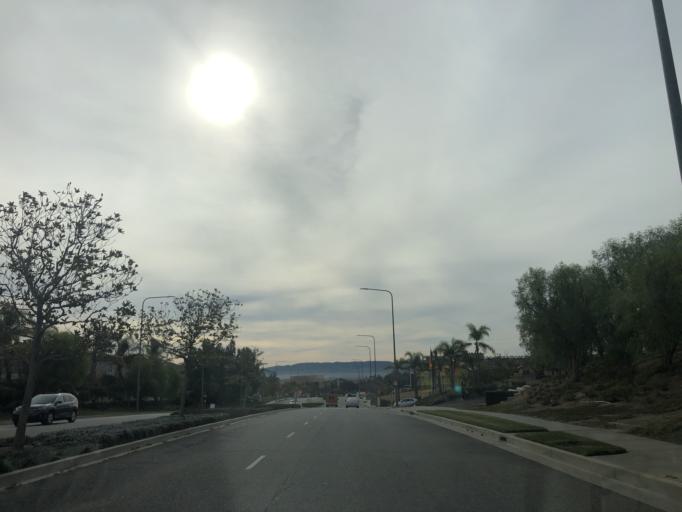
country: US
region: California
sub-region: Los Angeles County
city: Chatsworth
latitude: 34.2794
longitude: -118.5713
